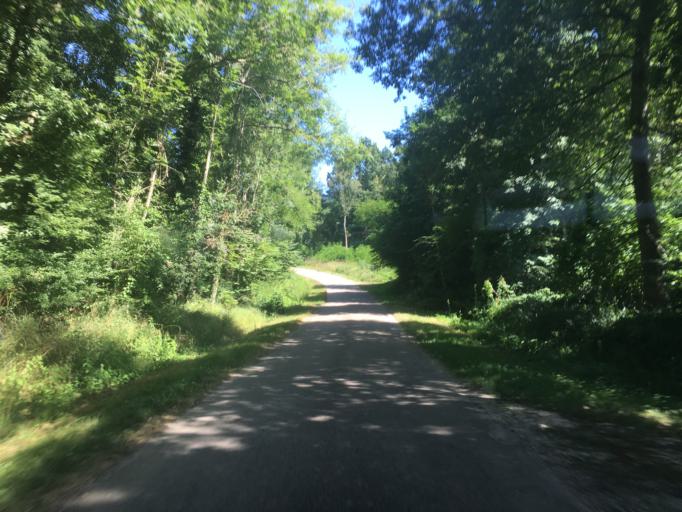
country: FR
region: Bourgogne
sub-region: Departement de l'Yonne
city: Fleury-la-Vallee
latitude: 47.8672
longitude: 3.4410
